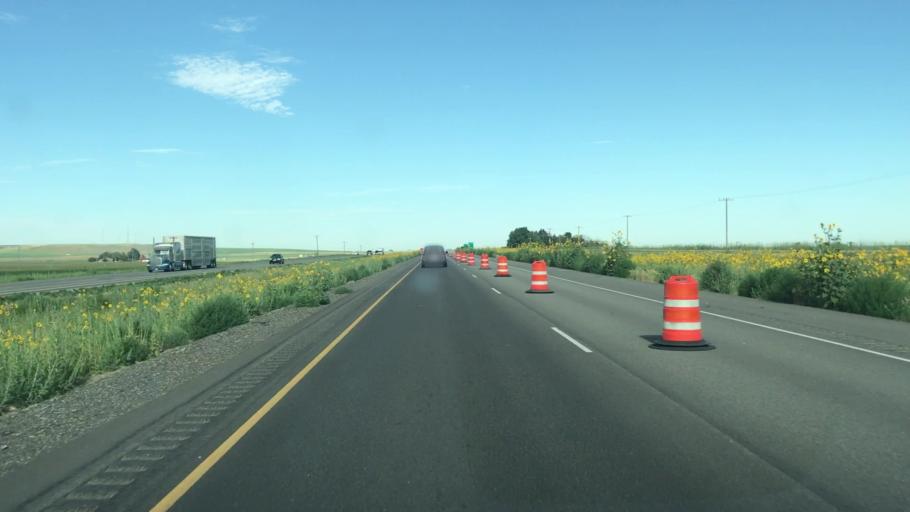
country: US
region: Idaho
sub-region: Cassia County
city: Burley
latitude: 42.5763
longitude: -114.0357
